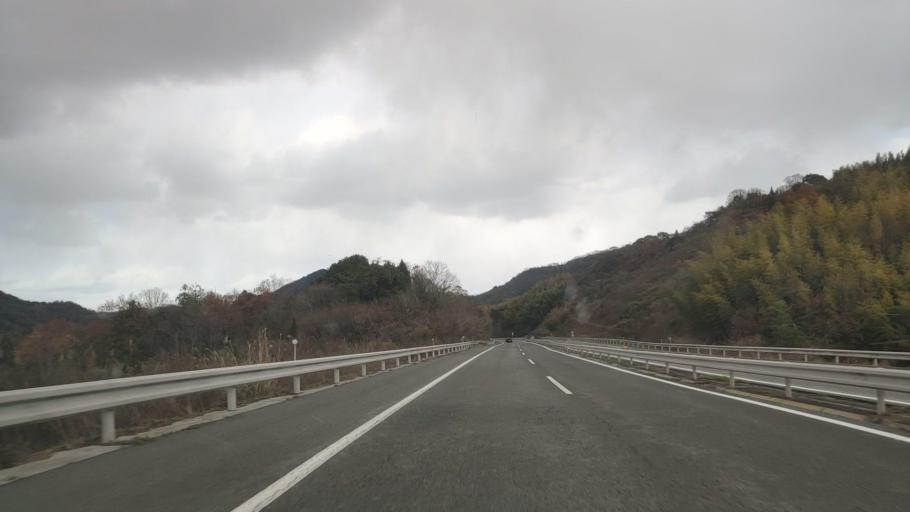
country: JP
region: Hiroshima
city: Innoshima
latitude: 34.1414
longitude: 133.0574
